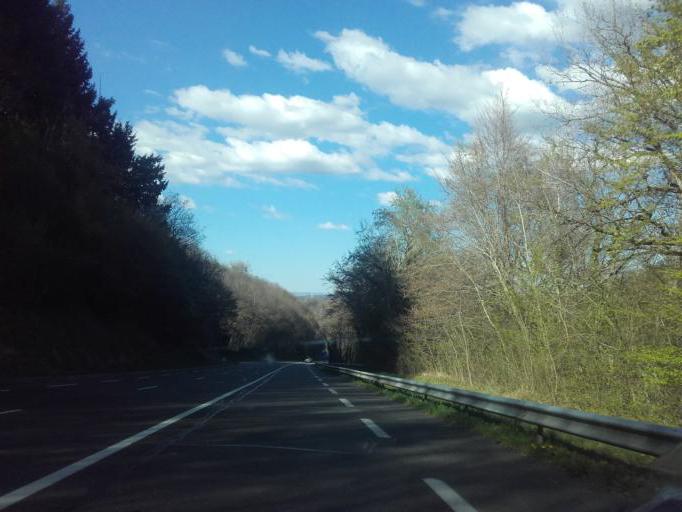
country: FR
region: Rhone-Alpes
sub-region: Departement de l'Isere
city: Nivolas-Vermelle
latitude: 45.5233
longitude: 5.3039
